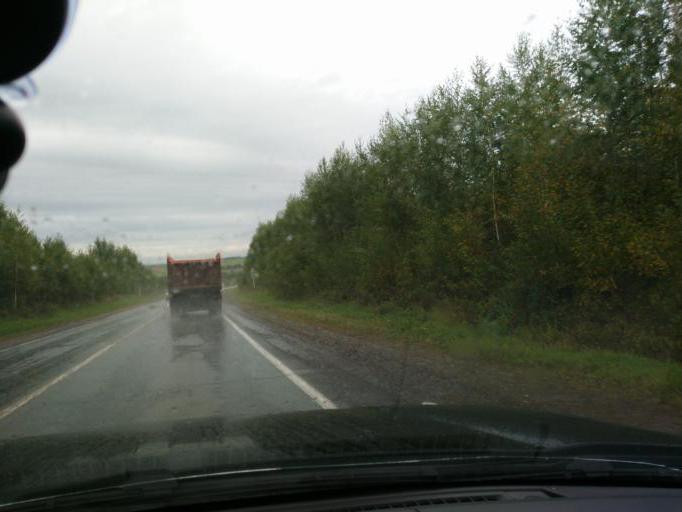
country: RU
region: Perm
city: Kultayevo
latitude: 57.8466
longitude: 55.8343
